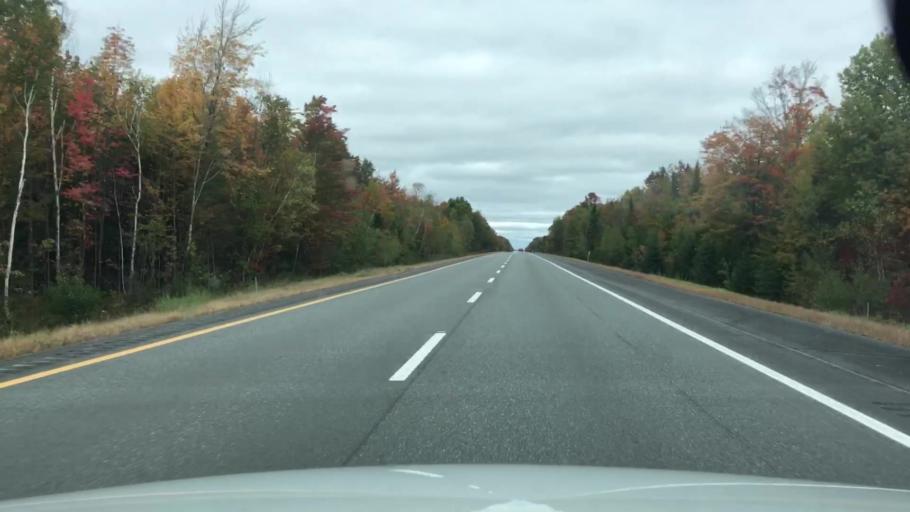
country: US
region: Maine
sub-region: Waldo County
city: Burnham
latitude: 44.7158
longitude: -69.4456
